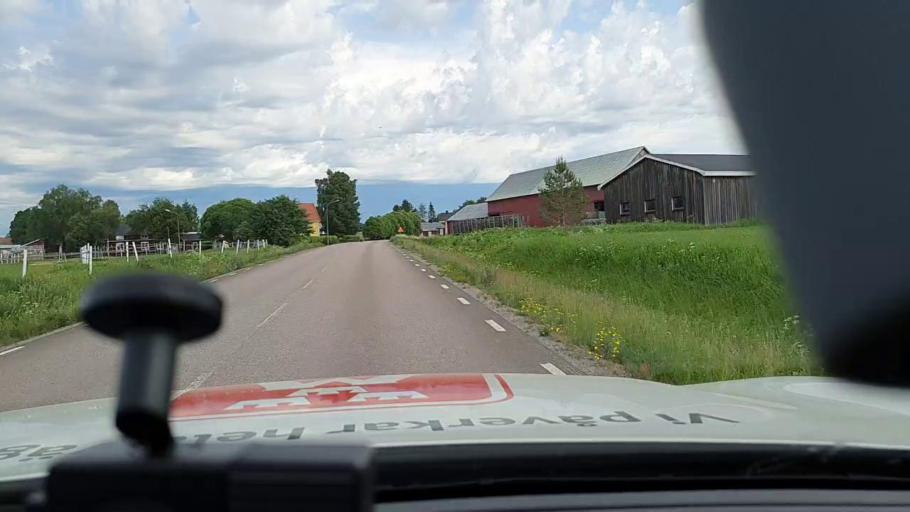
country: SE
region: Norrbotten
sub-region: Bodens Kommun
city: Saevast
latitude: 65.7078
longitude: 21.7614
